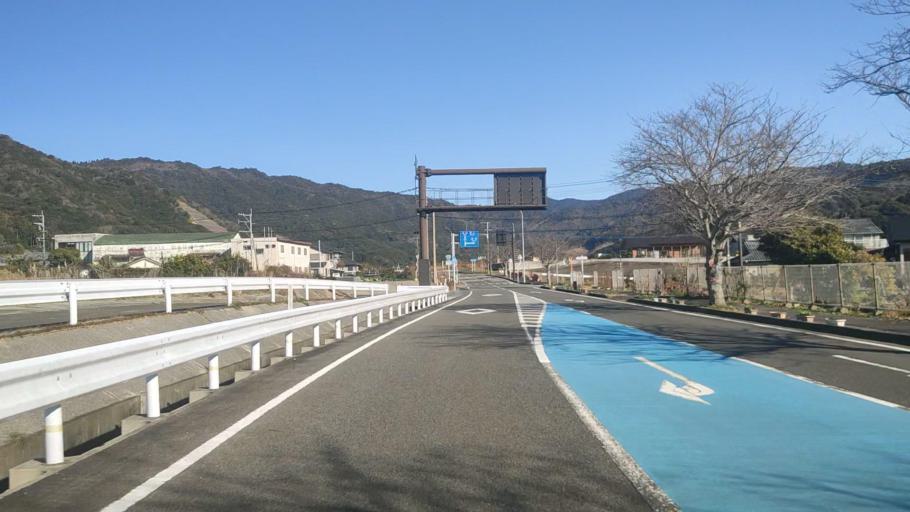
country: JP
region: Miyazaki
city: Nobeoka
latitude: 32.7105
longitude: 131.8199
